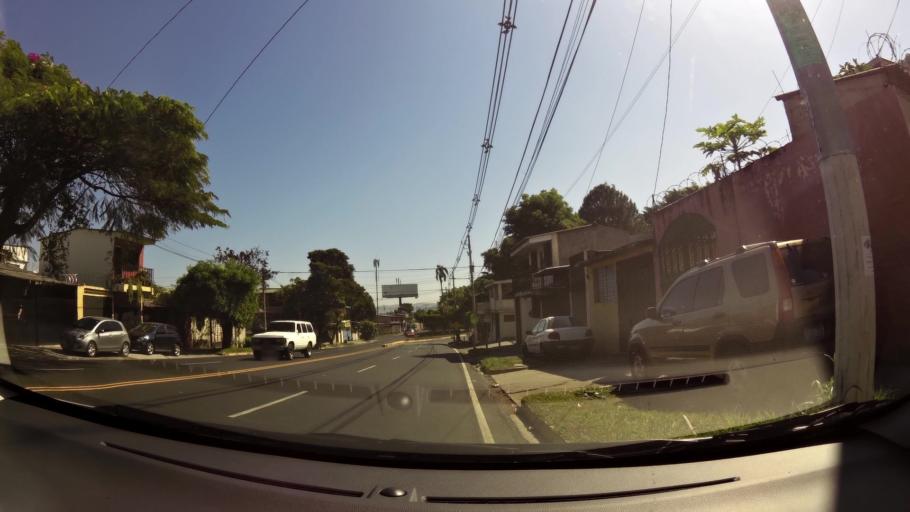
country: SV
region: La Libertad
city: Santa Tecla
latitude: 13.6665
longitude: -89.2861
